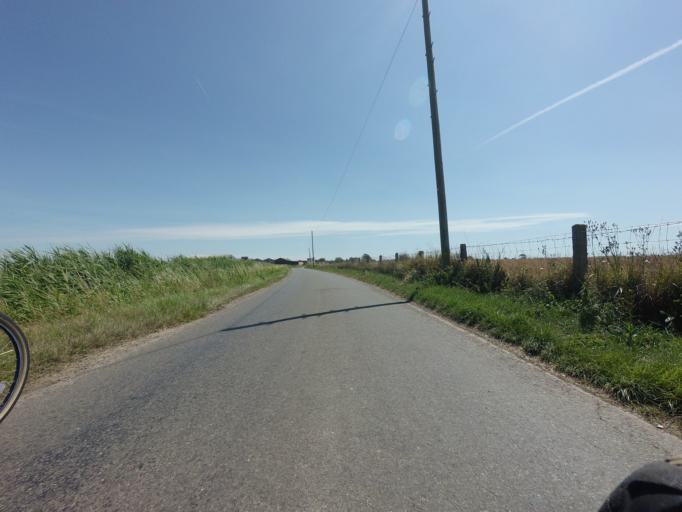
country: GB
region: England
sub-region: Kent
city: Lydd
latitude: 50.9671
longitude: 0.8962
